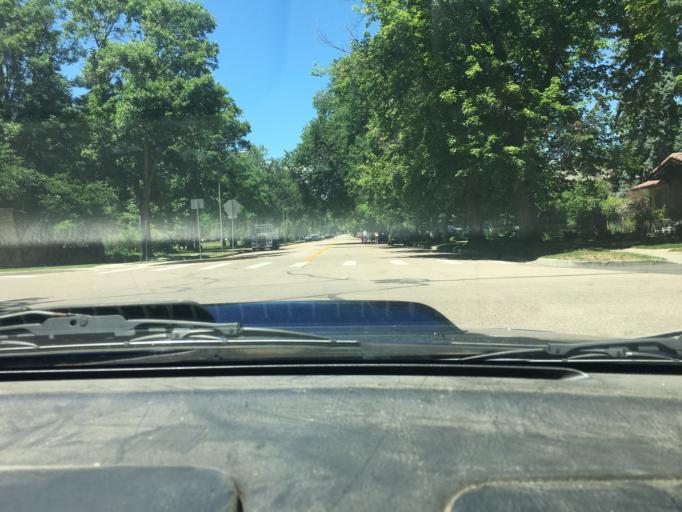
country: US
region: Colorado
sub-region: Larimer County
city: Fort Collins
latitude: 40.5857
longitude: -105.0991
